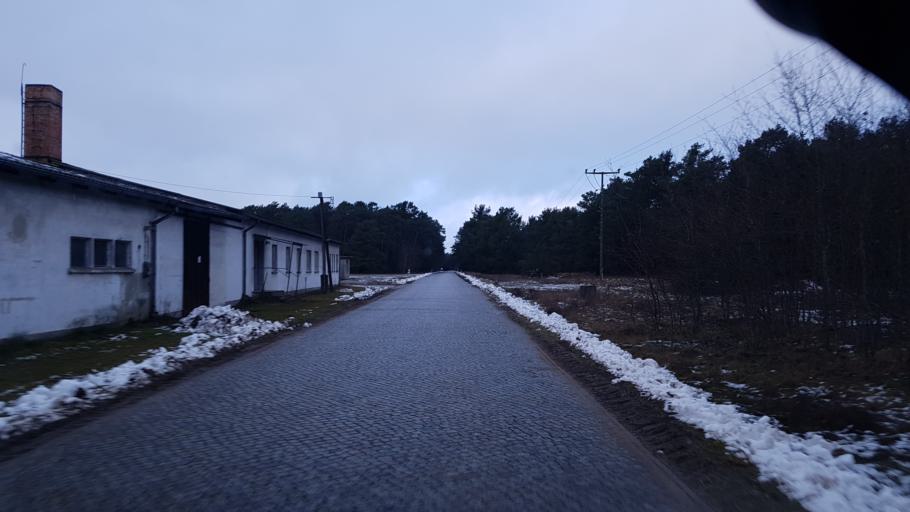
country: DE
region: Brandenburg
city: Janschwalde
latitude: 51.8704
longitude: 14.5090
